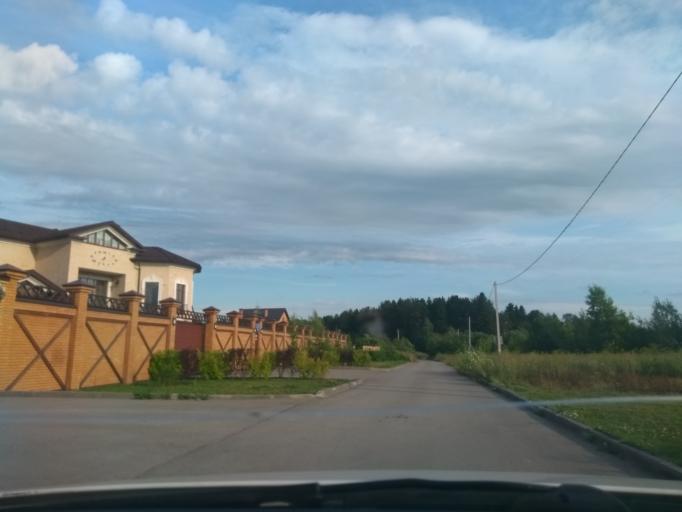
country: RU
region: Perm
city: Perm
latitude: 57.9992
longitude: 56.3274
